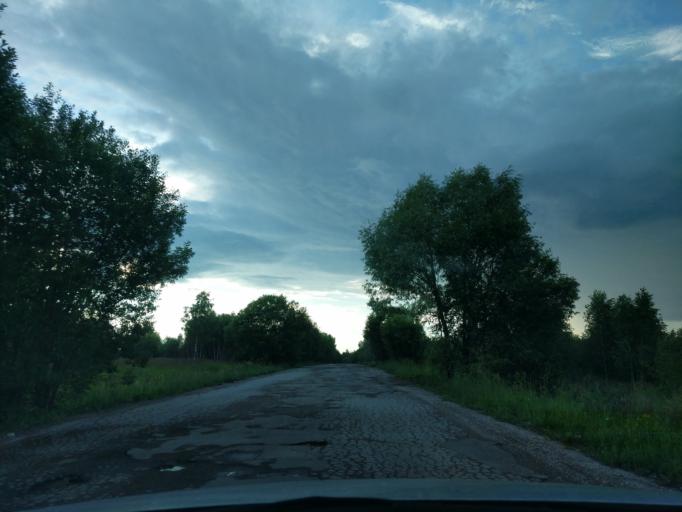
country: RU
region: Kaluga
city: Myatlevo
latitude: 54.8554
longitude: 35.5812
